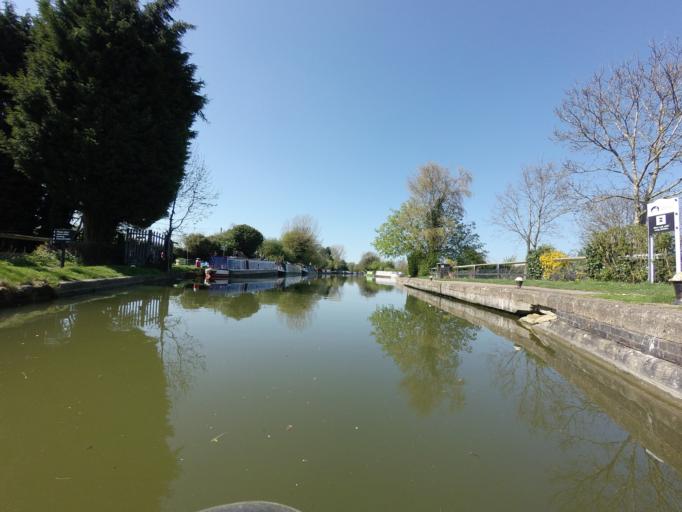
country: GB
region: England
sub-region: Hertfordshire
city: Tring
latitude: 51.7837
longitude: -0.6123
